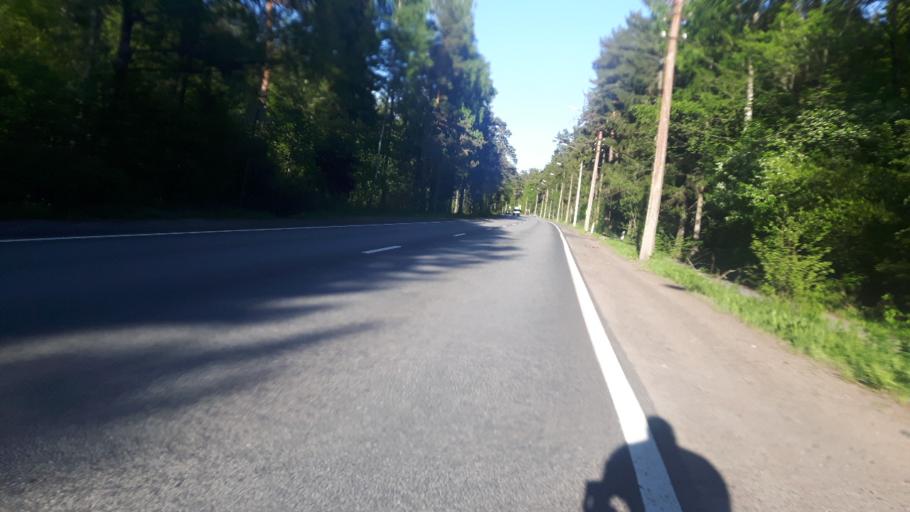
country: RU
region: Leningrad
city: Molodezhnoye
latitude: 60.1805
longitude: 29.4849
